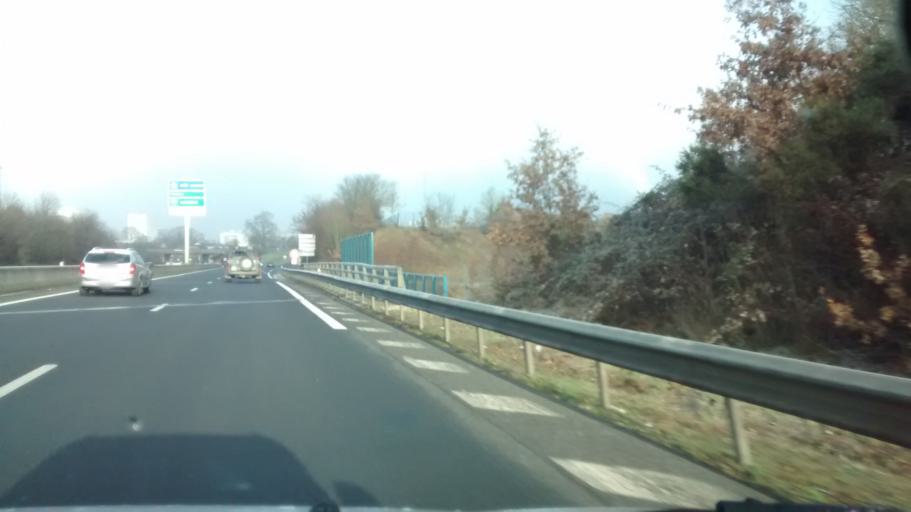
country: FR
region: Centre
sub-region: Departement d'Indre-et-Loire
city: Joue-les-Tours
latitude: 47.3369
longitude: 0.6697
